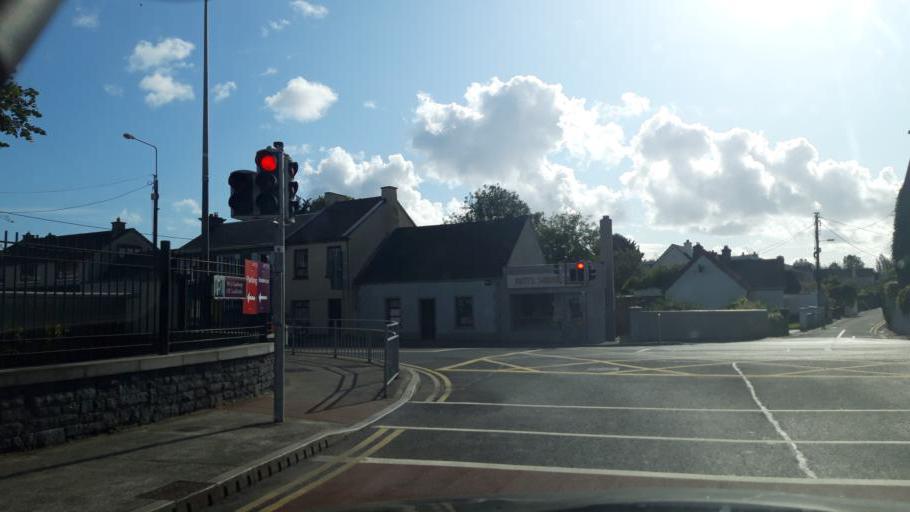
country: IE
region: Connaught
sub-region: County Galway
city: Gaillimh
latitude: 53.2813
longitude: -9.0643
